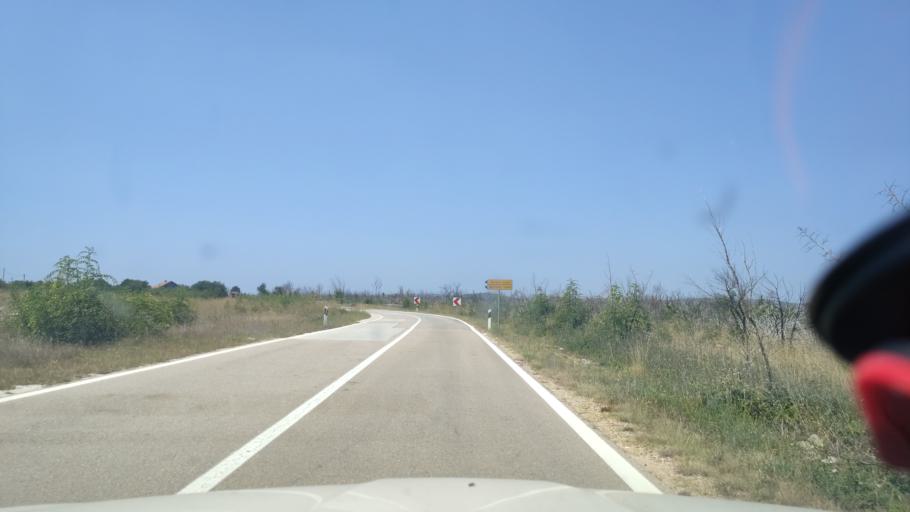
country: HR
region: Sibensko-Kniniska
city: Kistanje
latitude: 43.9770
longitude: 15.9270
